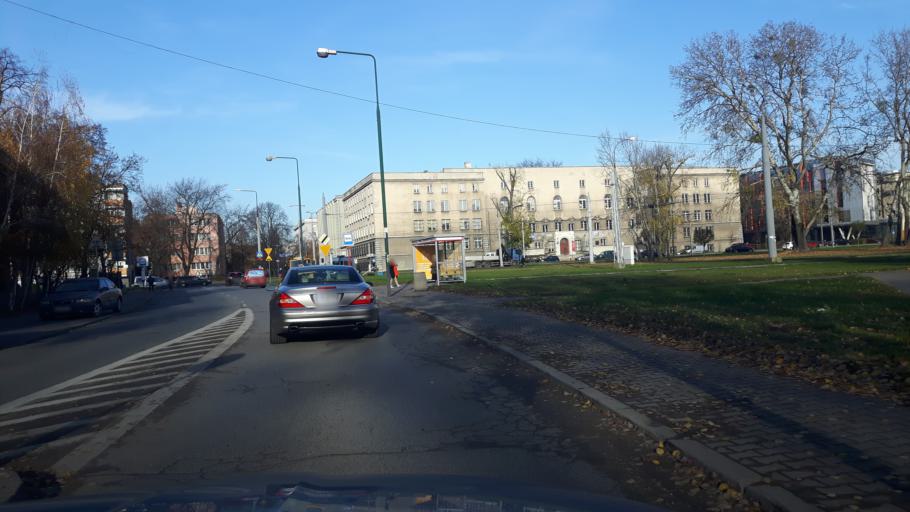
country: PL
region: Masovian Voivodeship
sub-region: Warszawa
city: Ochota
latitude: 52.2095
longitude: 20.9804
